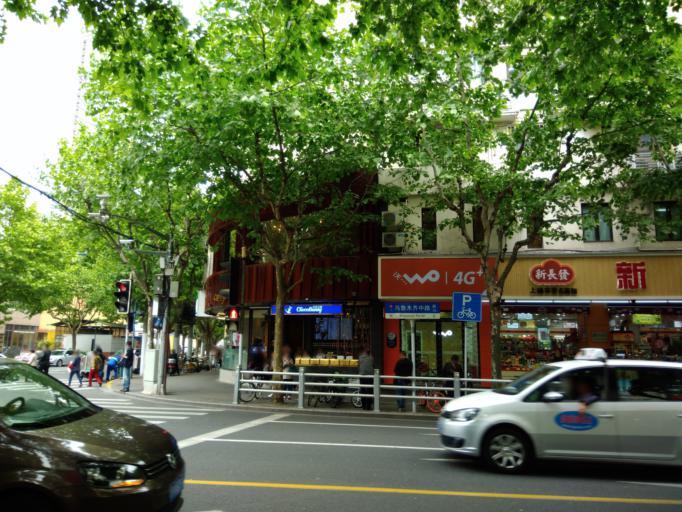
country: CN
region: Shanghai Shi
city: Changning
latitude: 31.2187
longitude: 121.4393
